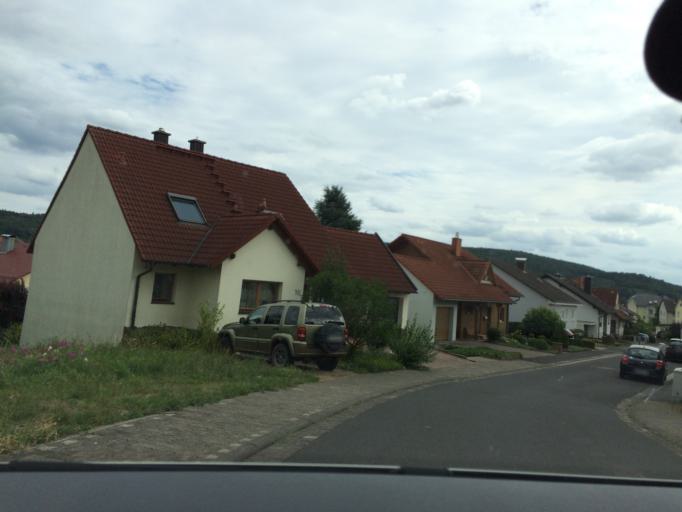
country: DE
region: Bavaria
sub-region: Regierungsbezirk Unterfranken
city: Hosbach
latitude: 50.0076
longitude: 9.1998
